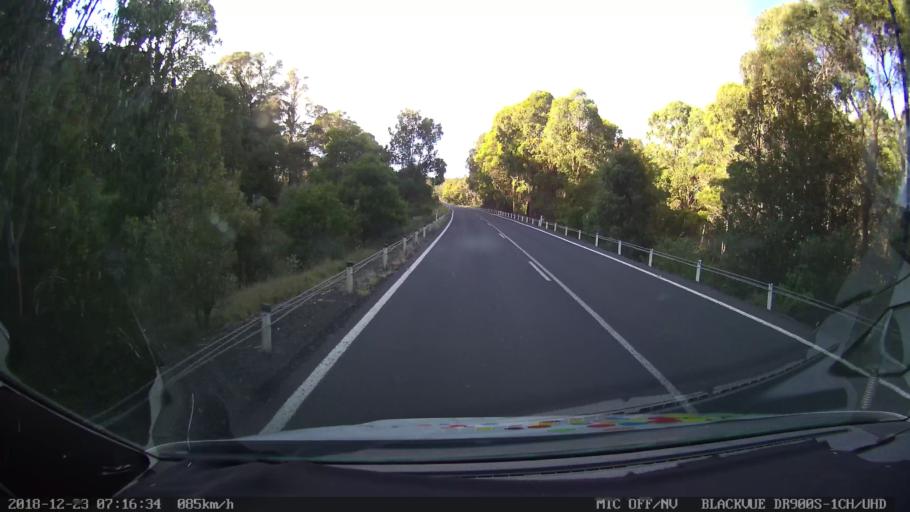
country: AU
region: New South Wales
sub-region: Bellingen
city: Dorrigo
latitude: -30.4573
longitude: 152.3087
